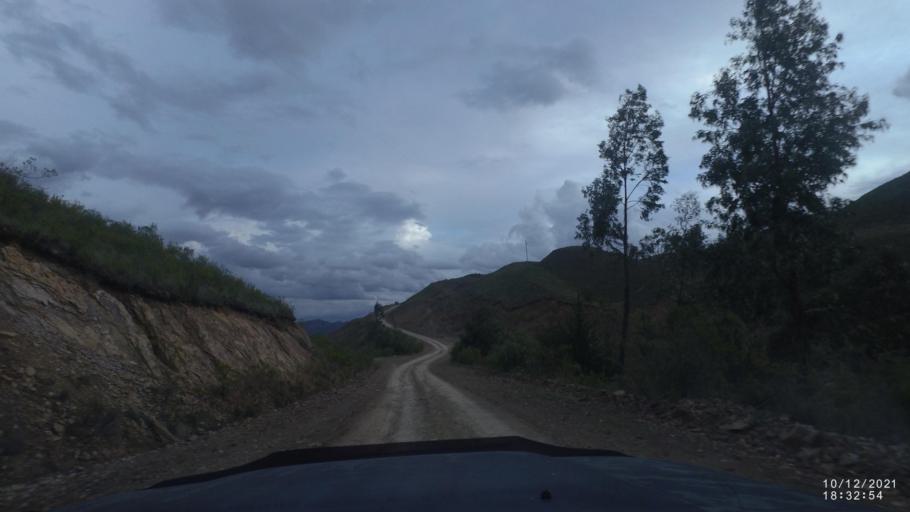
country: BO
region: Cochabamba
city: Tarata
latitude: -17.8181
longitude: -65.9872
